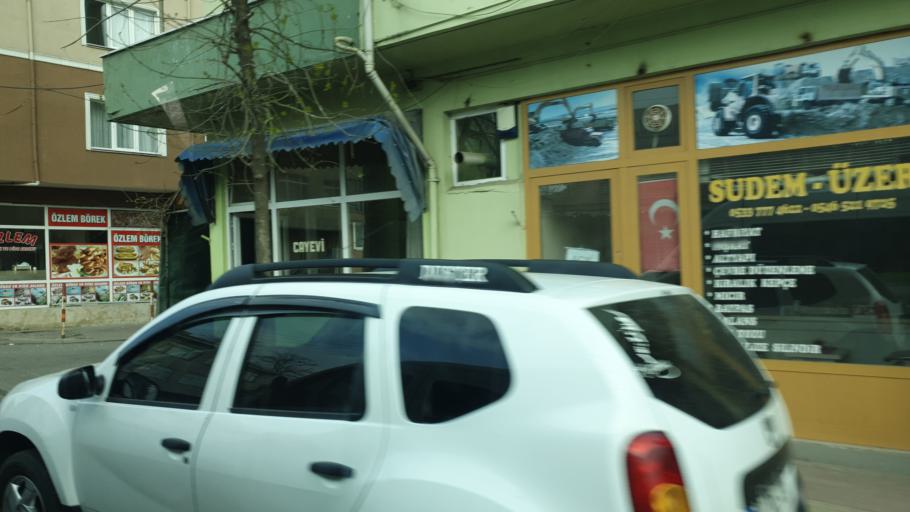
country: TR
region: Tekirdag
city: Muratli
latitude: 41.1750
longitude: 27.5004
